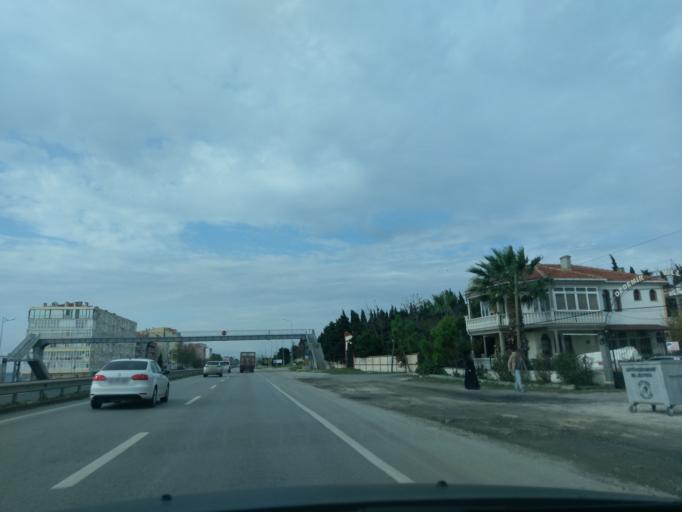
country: TR
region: Istanbul
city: Celaliye
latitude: 41.0456
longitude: 28.4082
